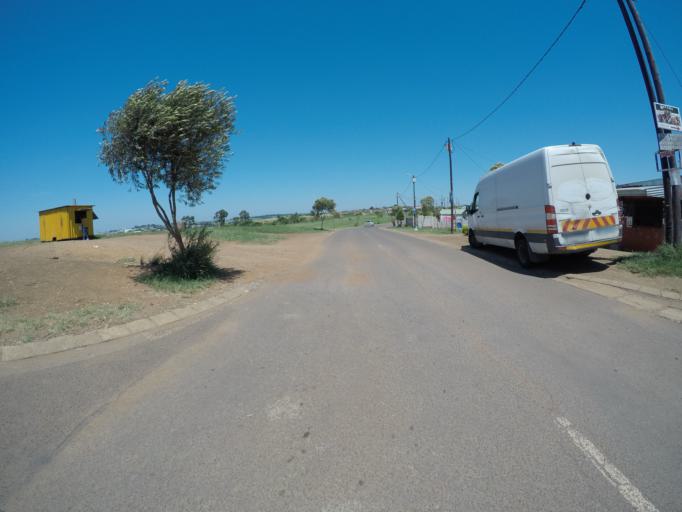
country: ZA
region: KwaZulu-Natal
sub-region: uThungulu District Municipality
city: Empangeni
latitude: -28.7663
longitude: 31.8799
